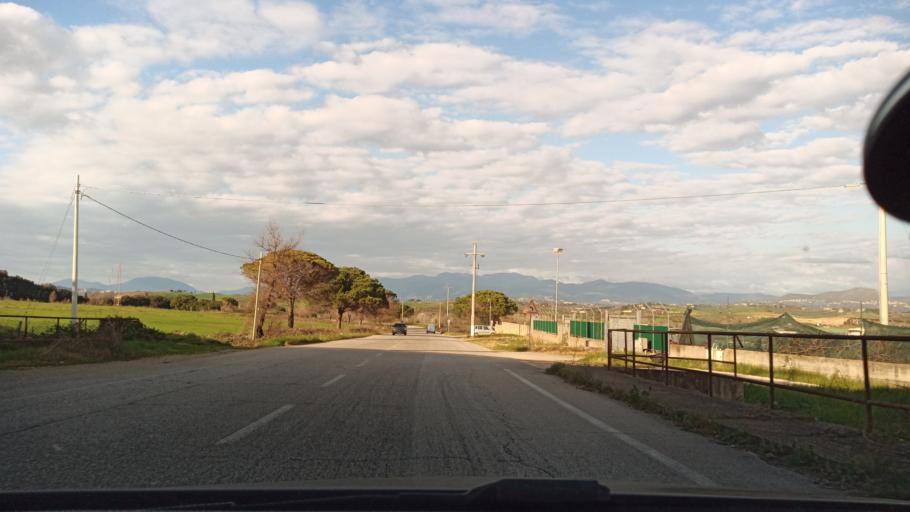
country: IT
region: Latium
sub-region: Citta metropolitana di Roma Capitale
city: Fiano Romano
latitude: 42.1615
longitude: 12.6203
